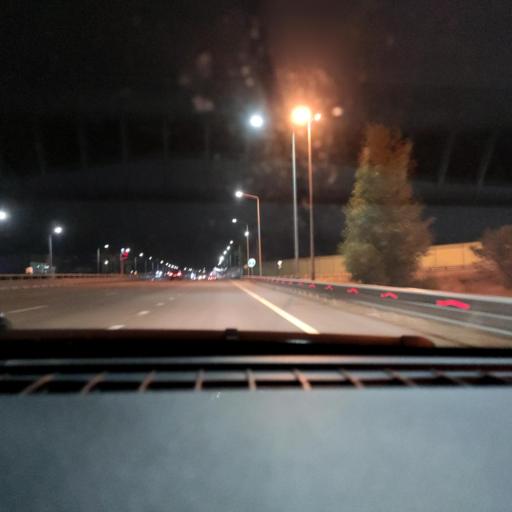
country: RU
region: Voronezj
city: Somovo
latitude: 51.6791
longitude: 39.3017
